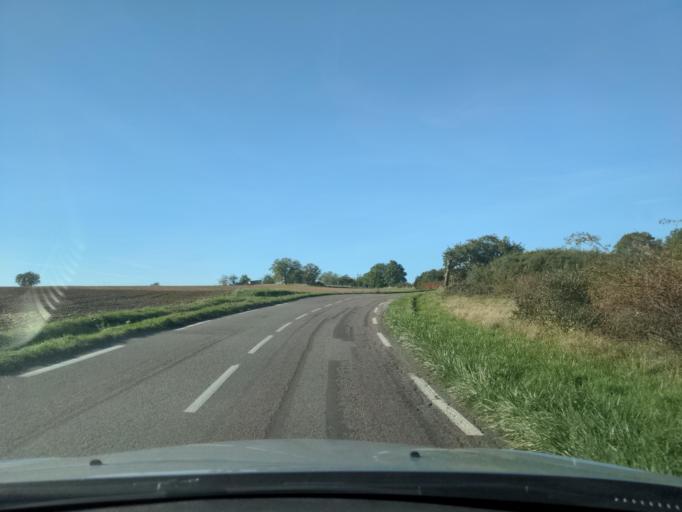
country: FR
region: Bourgogne
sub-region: Departement de la Cote-d'Or
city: Ruffey-les-Echirey
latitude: 47.3719
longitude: 5.0704
